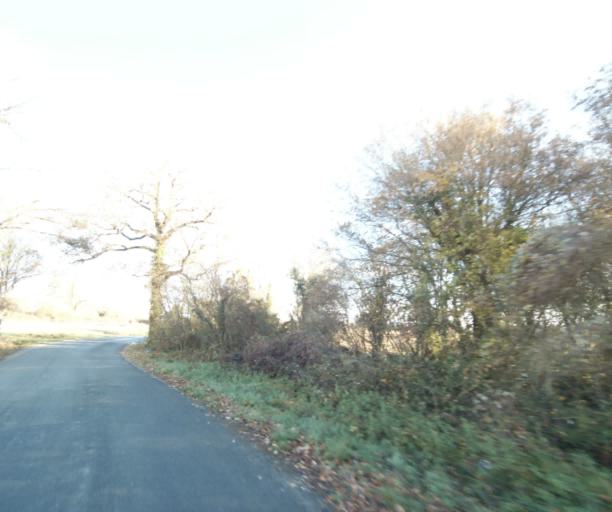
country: FR
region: Poitou-Charentes
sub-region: Departement de la Charente-Maritime
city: Fontcouverte
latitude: 45.7414
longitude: -0.5863
